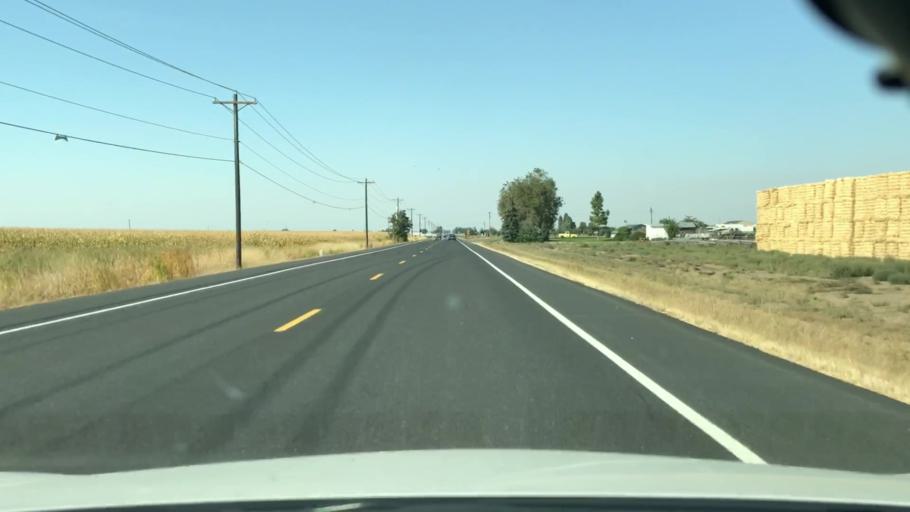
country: US
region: Washington
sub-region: Grant County
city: Moses Lake
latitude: 47.1199
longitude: -119.2359
